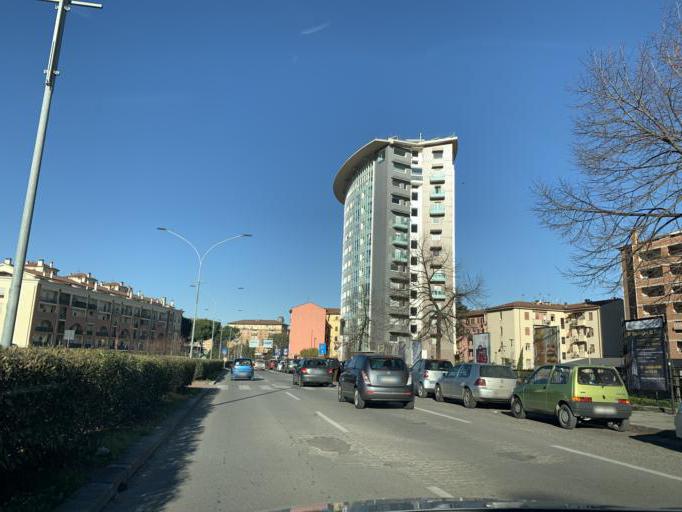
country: IT
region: Umbria
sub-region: Provincia di Terni
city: Terni
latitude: 42.5597
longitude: 12.6541
